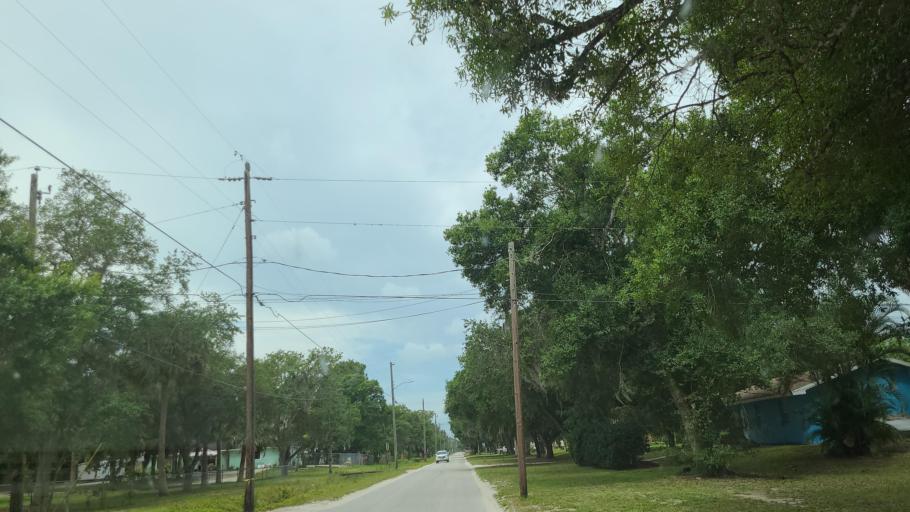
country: US
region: Florida
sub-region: Indian River County
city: Fellsmere
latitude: 27.7717
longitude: -80.5964
